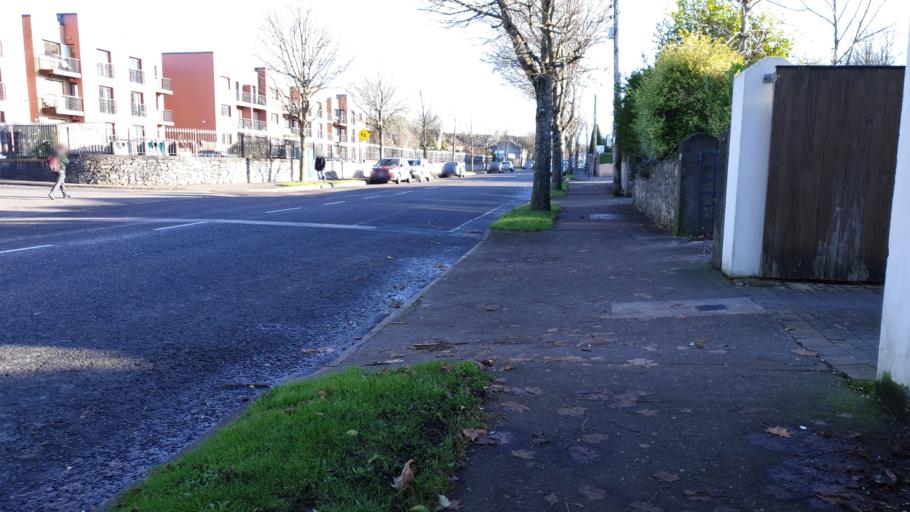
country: IE
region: Munster
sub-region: County Cork
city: Cork
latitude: 51.8912
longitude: -8.4493
